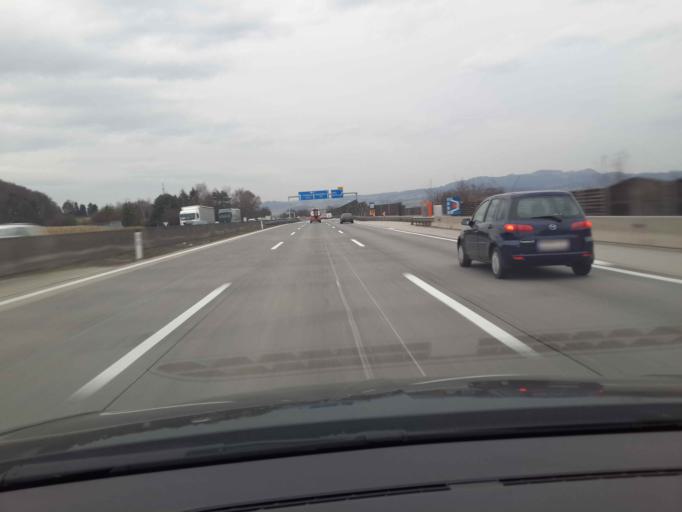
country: AT
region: Lower Austria
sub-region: Politischer Bezirk Scheibbs
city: Wieselburg
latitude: 48.1601
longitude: 15.1229
